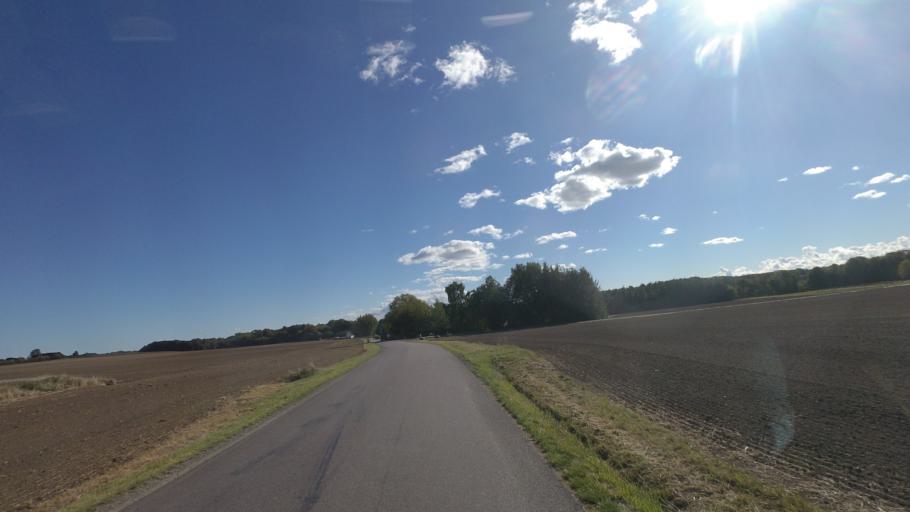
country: DK
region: Capital Region
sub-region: Bornholm Kommune
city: Akirkeby
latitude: 55.1362
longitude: 15.0180
